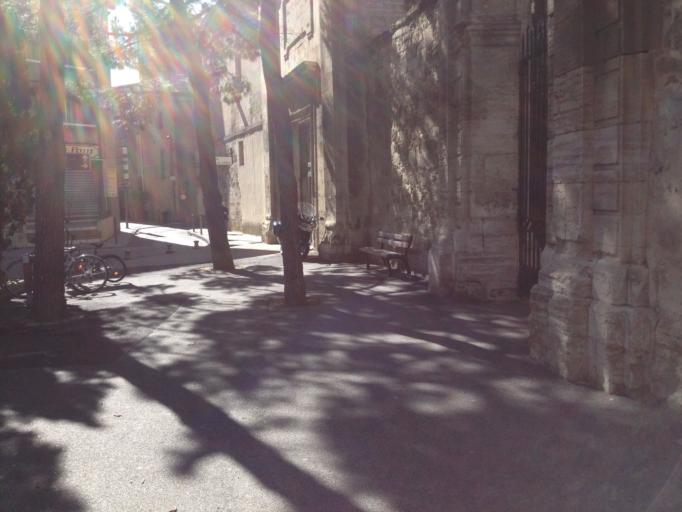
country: FR
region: Provence-Alpes-Cote d'Azur
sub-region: Departement du Vaucluse
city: Avignon
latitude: 43.9529
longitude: 4.8058
